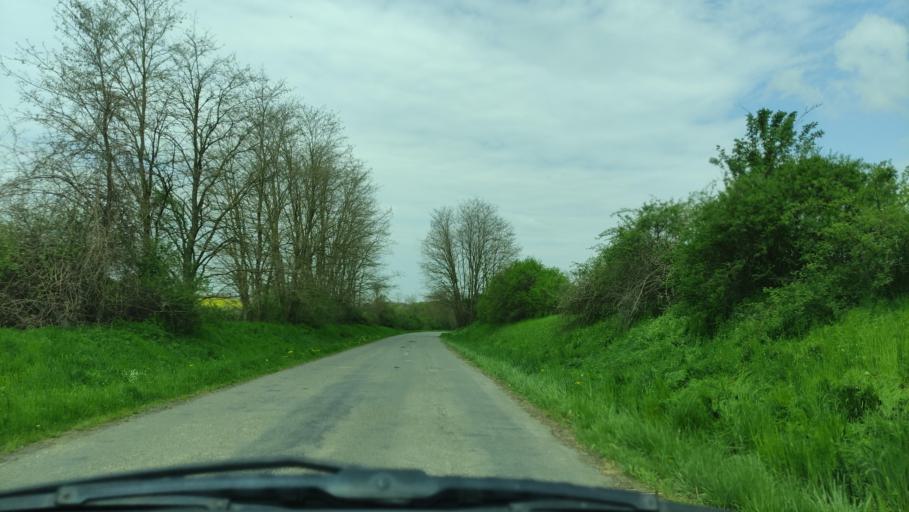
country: HU
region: Baranya
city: Magocs
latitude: 46.3000
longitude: 18.1723
